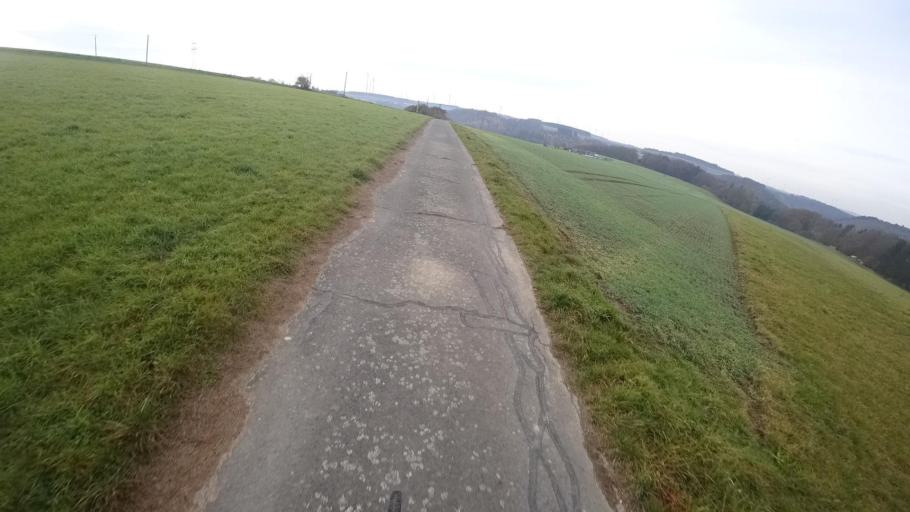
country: DE
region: Rheinland-Pfalz
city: Schwall
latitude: 50.1431
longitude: 7.5501
